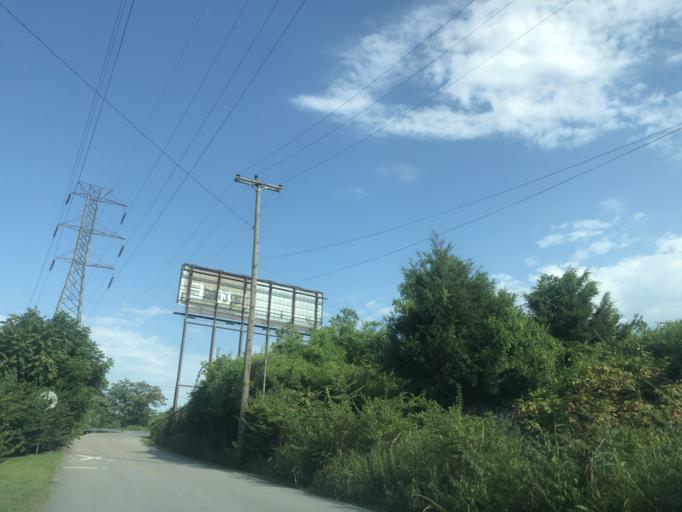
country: US
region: Tennessee
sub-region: Davidson County
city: Nashville
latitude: 36.1563
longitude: -86.7624
